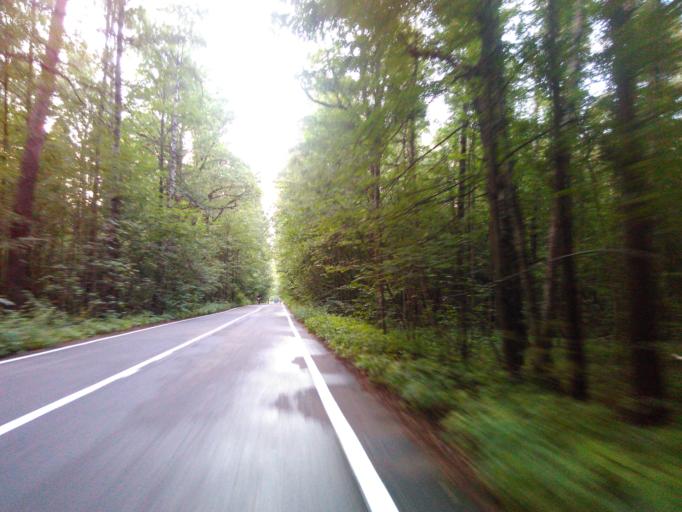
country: RU
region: Moskovskaya
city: Bogorodskoye
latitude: 55.8394
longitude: 37.7272
